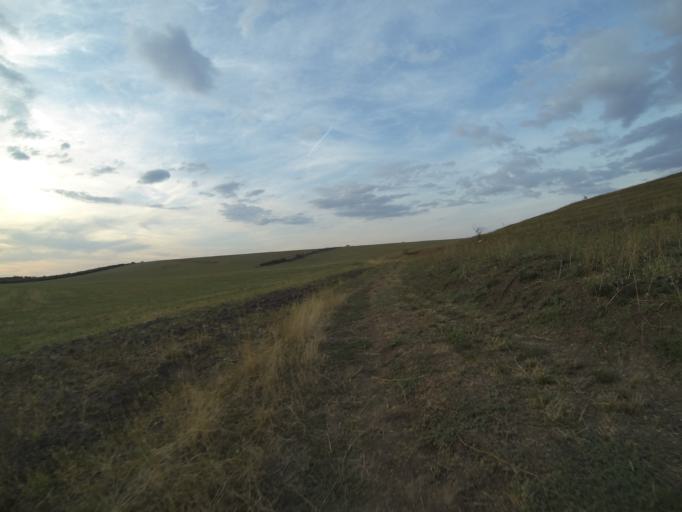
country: RO
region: Dolj
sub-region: Comuna Ceratu
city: Ceratu
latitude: 44.0950
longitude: 23.6653
